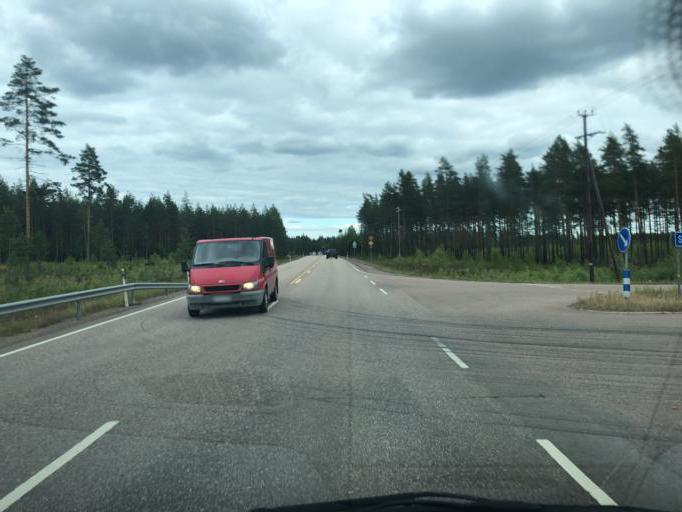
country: FI
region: Southern Savonia
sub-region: Mikkeli
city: Maentyharju
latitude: 61.0962
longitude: 27.0876
